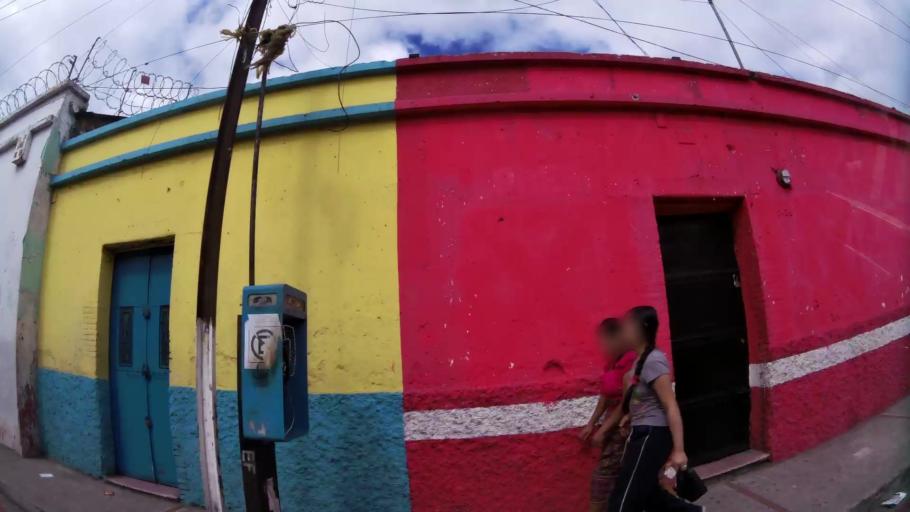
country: GT
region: Guatemala
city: Mixco
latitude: 14.6313
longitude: -90.6073
